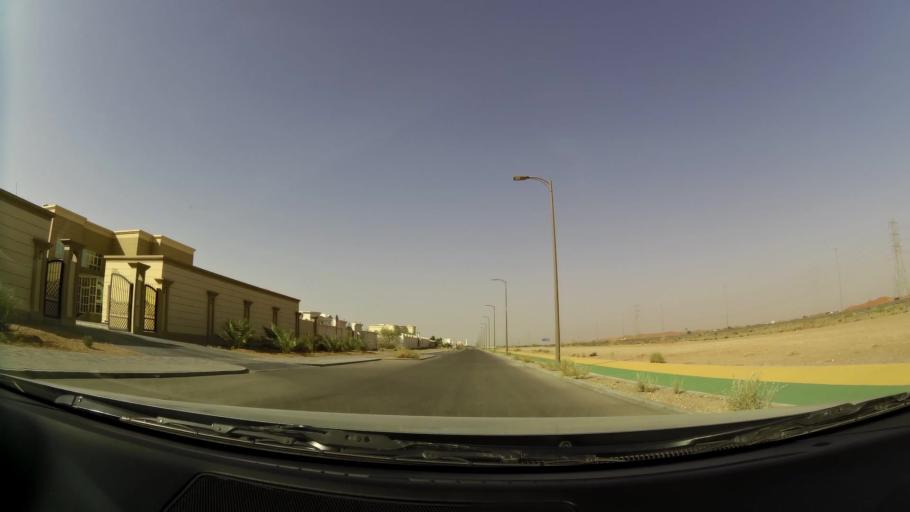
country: OM
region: Al Buraimi
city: Al Buraymi
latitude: 24.3627
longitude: 55.7906
